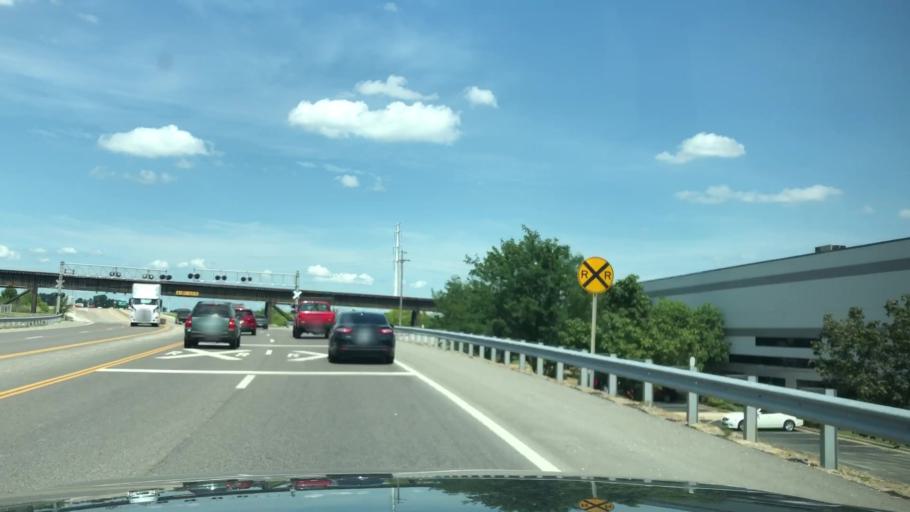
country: US
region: Missouri
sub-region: Saint Charles County
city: Saint Charles
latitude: 38.7890
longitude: -90.4557
